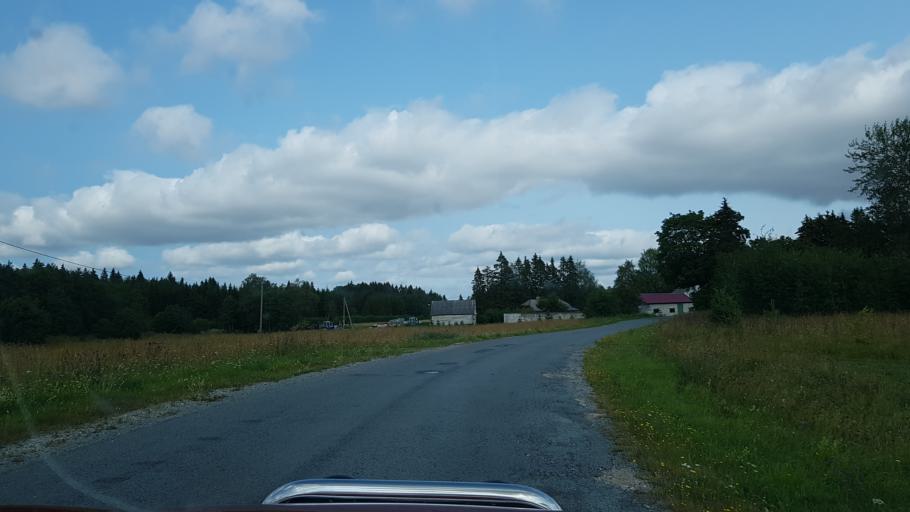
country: EE
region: Laeaene-Virumaa
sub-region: Kadrina vald
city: Kadrina
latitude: 59.3316
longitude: 26.0408
